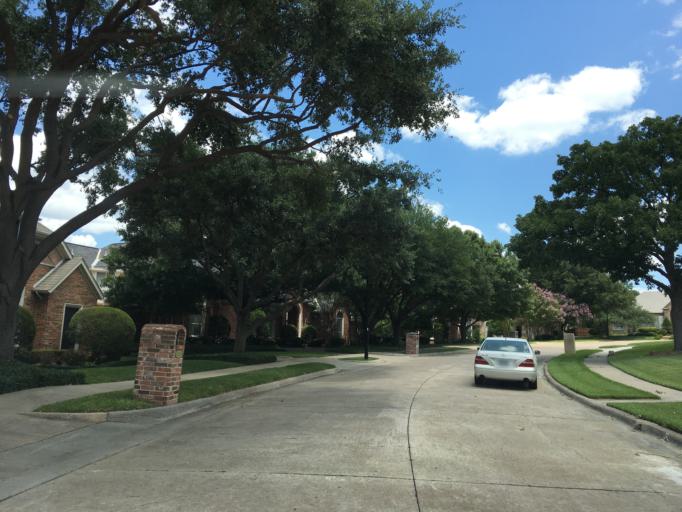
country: US
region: Texas
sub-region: Dallas County
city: Farmers Branch
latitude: 32.9266
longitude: -96.8576
